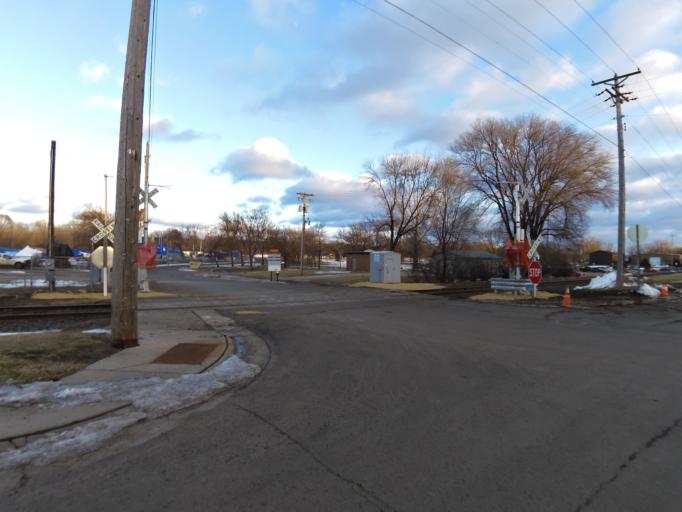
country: US
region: Minnesota
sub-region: Washington County
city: Bayport
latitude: 45.0172
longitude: -92.7763
